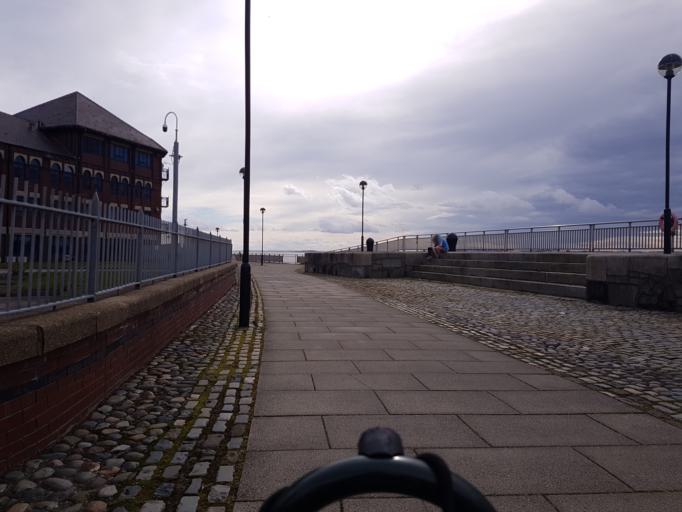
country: GB
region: England
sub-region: Metropolitan Borough of Wirral
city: New Ferry
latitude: 53.3779
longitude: -2.9725
